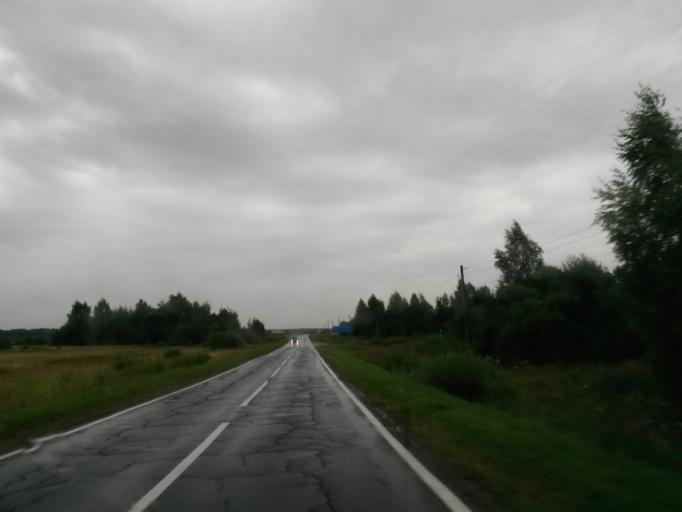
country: RU
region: Jaroslavl
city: Tutayev
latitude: 57.9493
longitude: 39.4564
